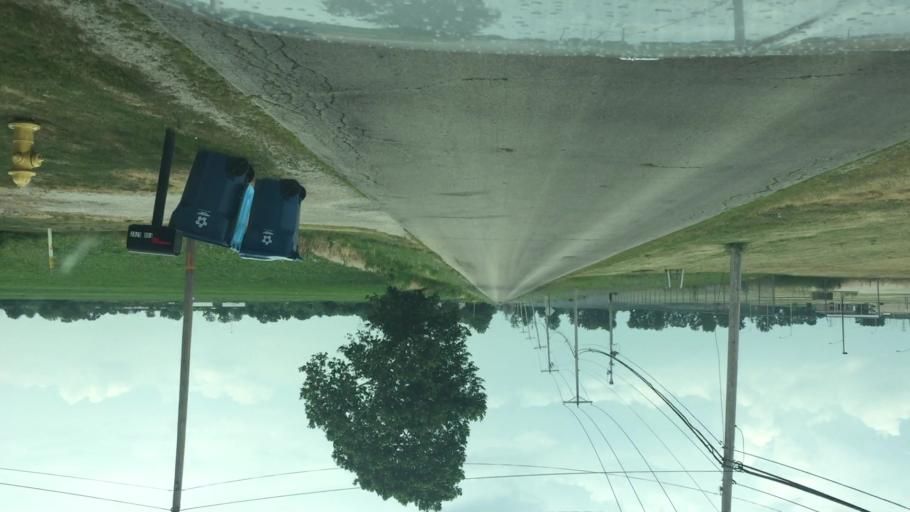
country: US
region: Ohio
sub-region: Wood County
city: Walbridge
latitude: 41.5880
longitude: -83.5271
